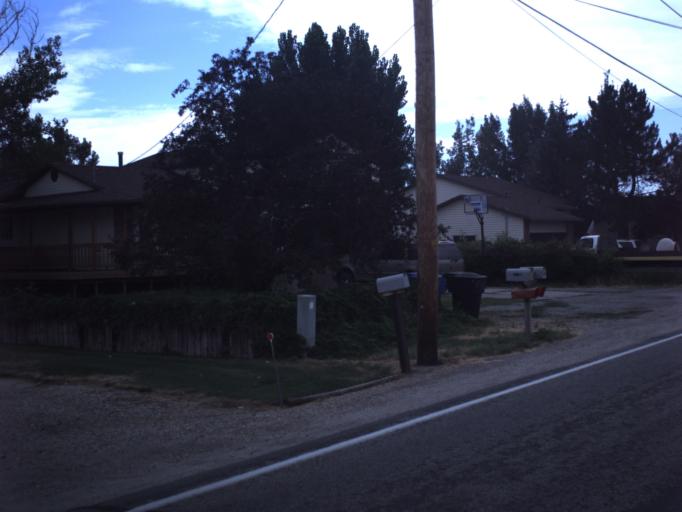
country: US
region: Utah
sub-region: Davis County
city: West Point
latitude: 41.1238
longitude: -112.1126
